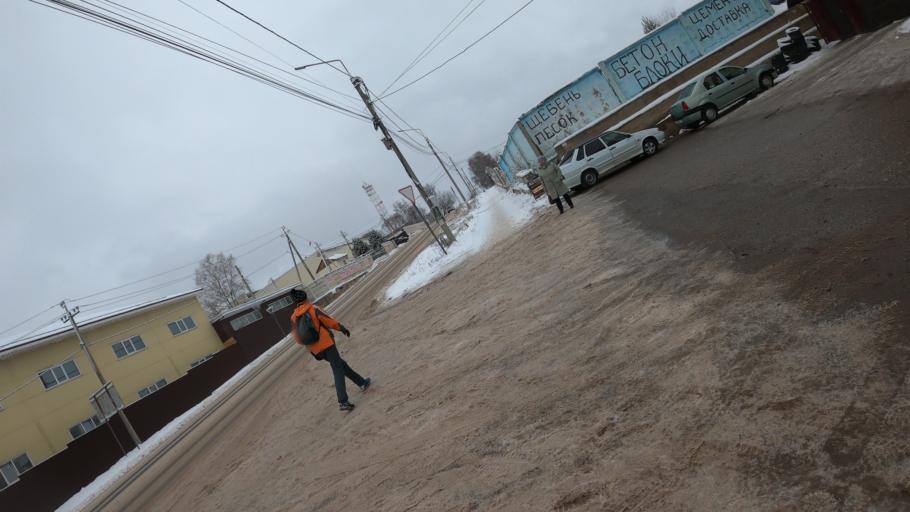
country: RU
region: Jaroslavl
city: Pereslavl'-Zalesskiy
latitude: 56.7414
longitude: 38.8916
